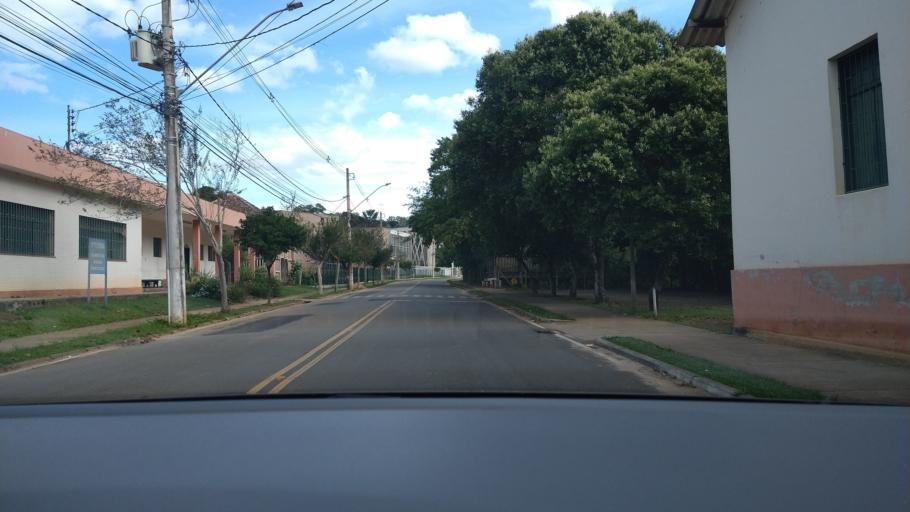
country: BR
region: Minas Gerais
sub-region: Vicosa
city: Vicosa
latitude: -20.7679
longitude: -42.8706
